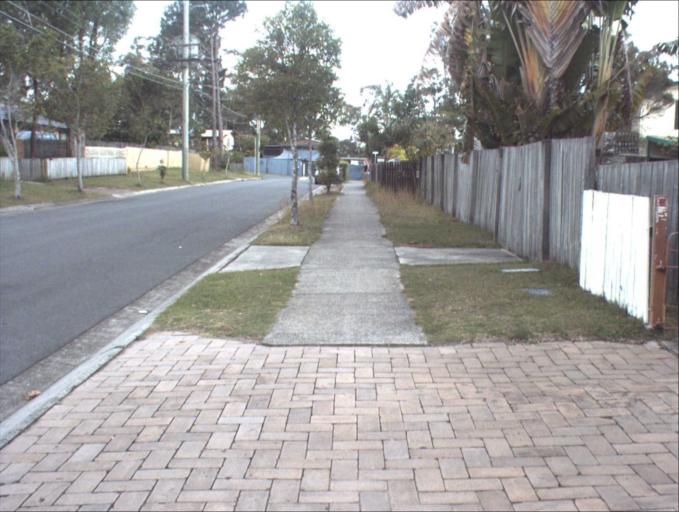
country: AU
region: Queensland
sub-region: Logan
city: Woodridge
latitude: -27.6336
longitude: 153.1047
